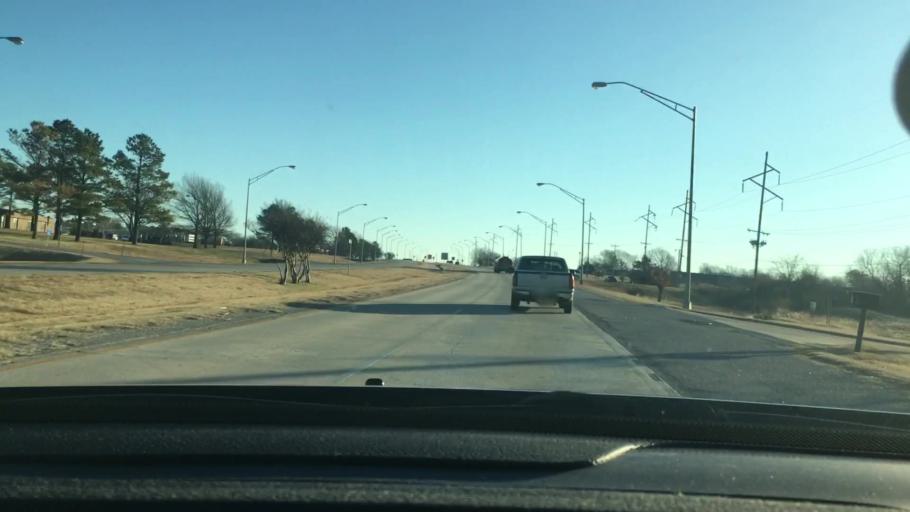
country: US
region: Oklahoma
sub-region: Carter County
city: Ardmore
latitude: 34.2020
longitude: -97.1535
